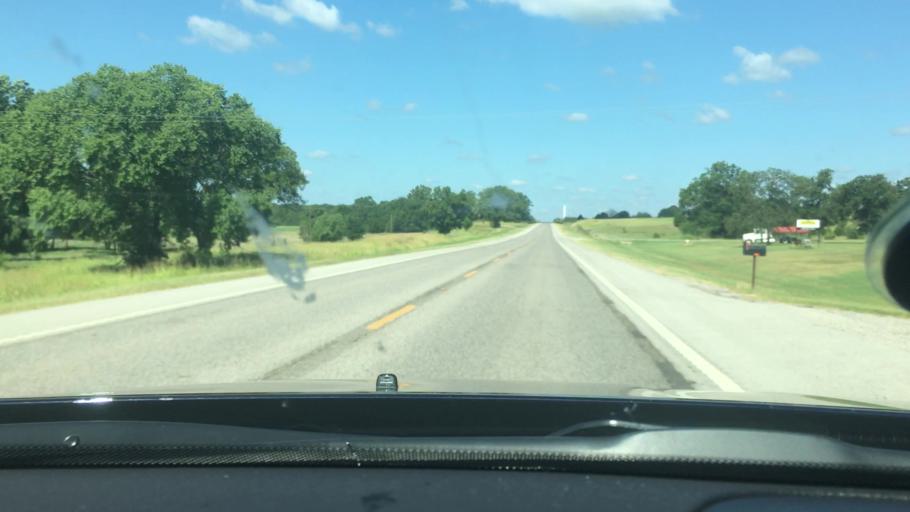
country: US
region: Oklahoma
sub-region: Carter County
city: Dickson
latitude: 34.1003
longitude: -96.9224
